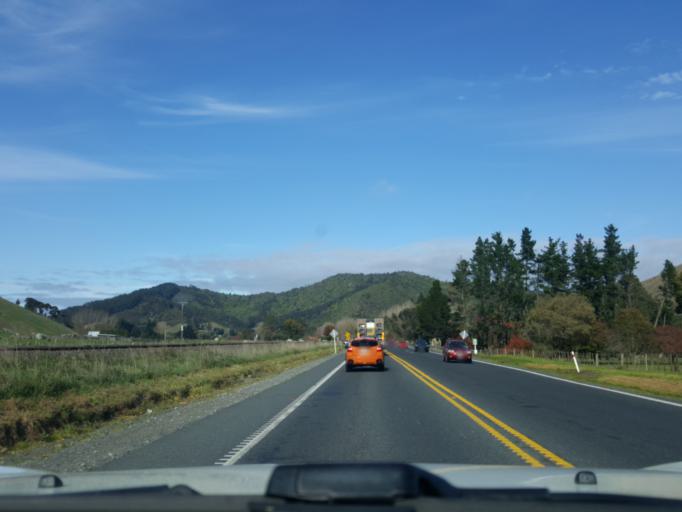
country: NZ
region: Waikato
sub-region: Waikato District
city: Ngaruawahia
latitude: -37.5889
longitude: 175.1594
